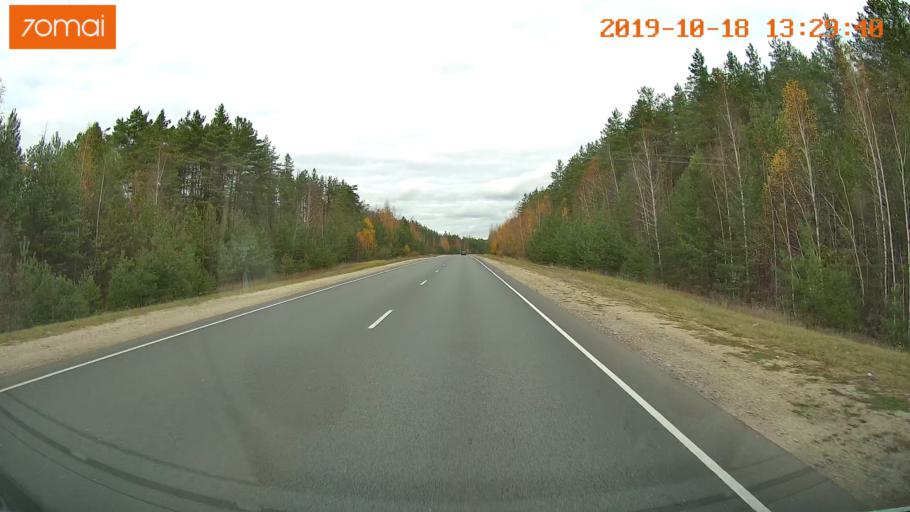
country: RU
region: Rjazan
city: Solotcha
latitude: 54.7983
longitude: 39.8765
